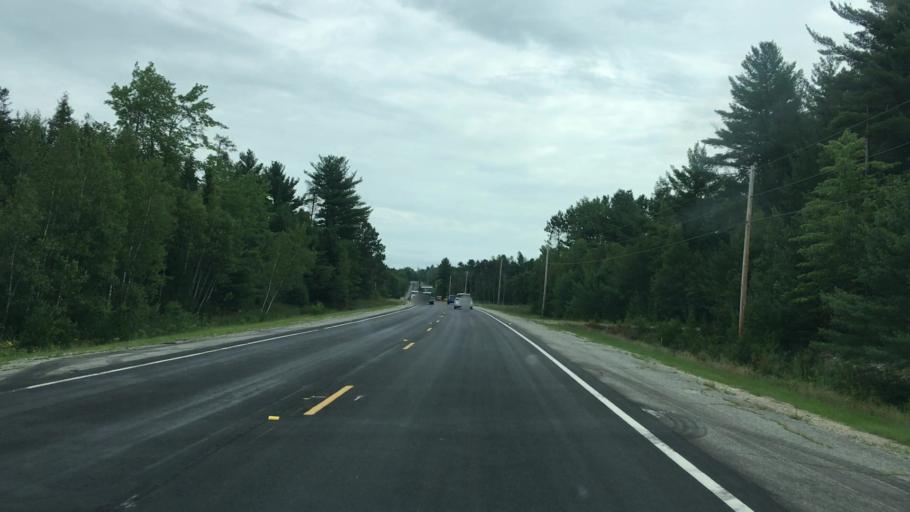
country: US
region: Maine
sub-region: Washington County
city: Addison
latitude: 44.9413
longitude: -67.7152
